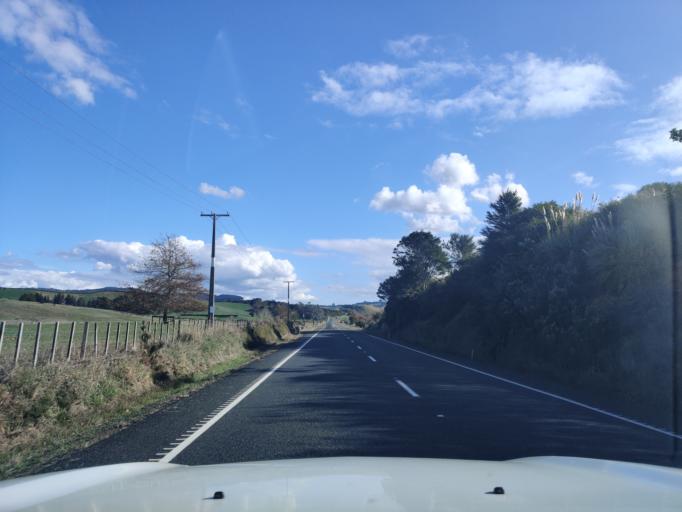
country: NZ
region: Waikato
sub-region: Hauraki District
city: Ngatea
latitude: -37.2848
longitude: 175.3955
